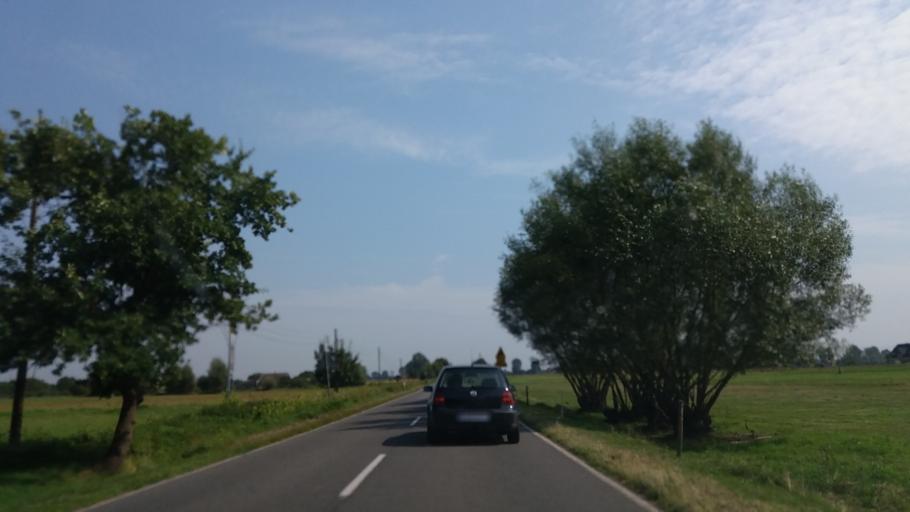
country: PL
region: Lubusz
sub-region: Powiat strzelecko-drezdenecki
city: Zwierzyn
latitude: 52.8212
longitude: 15.6221
